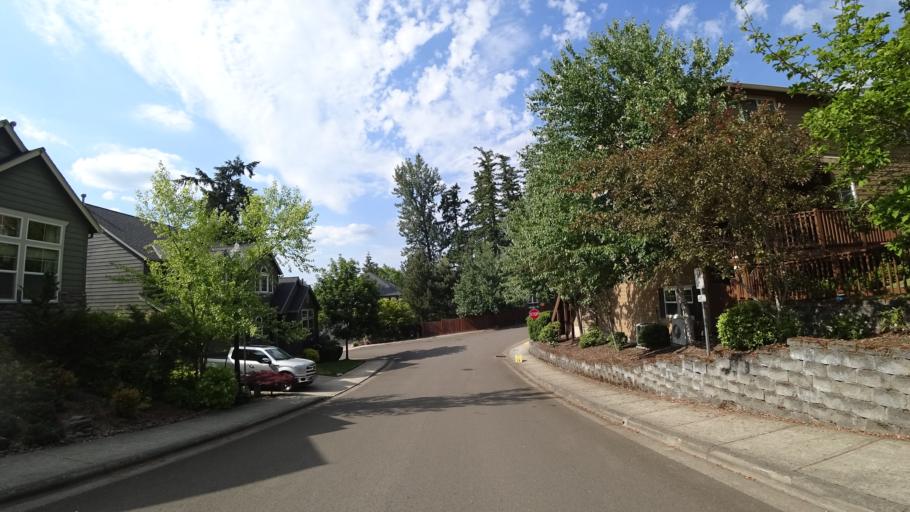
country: US
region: Oregon
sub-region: Washington County
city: Garden Home-Whitford
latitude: 45.4577
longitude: -122.7498
